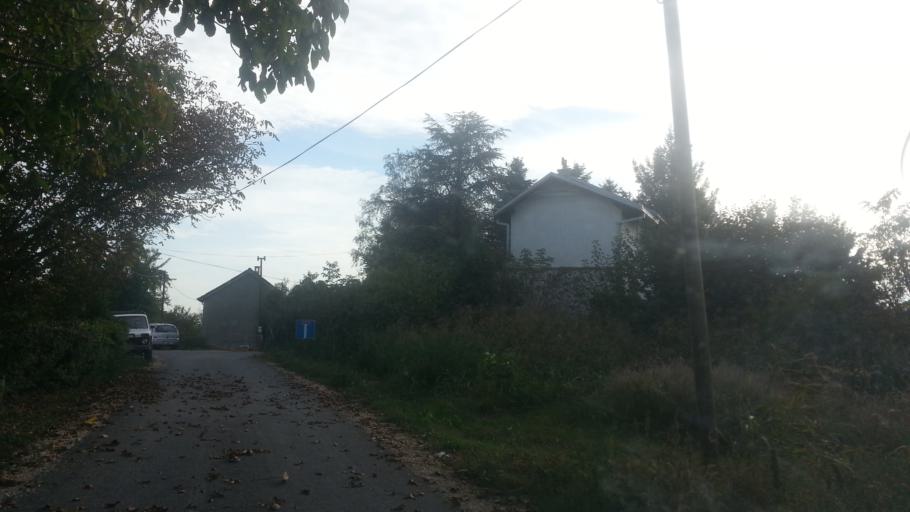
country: RS
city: Belegis
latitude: 45.0226
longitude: 20.3491
